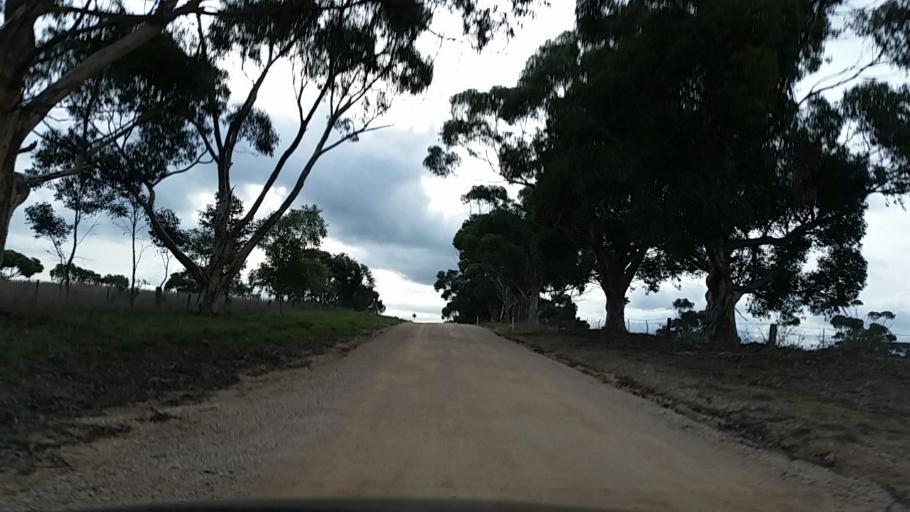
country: AU
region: South Australia
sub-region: Mount Barker
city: Nairne
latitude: -34.9808
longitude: 139.0357
